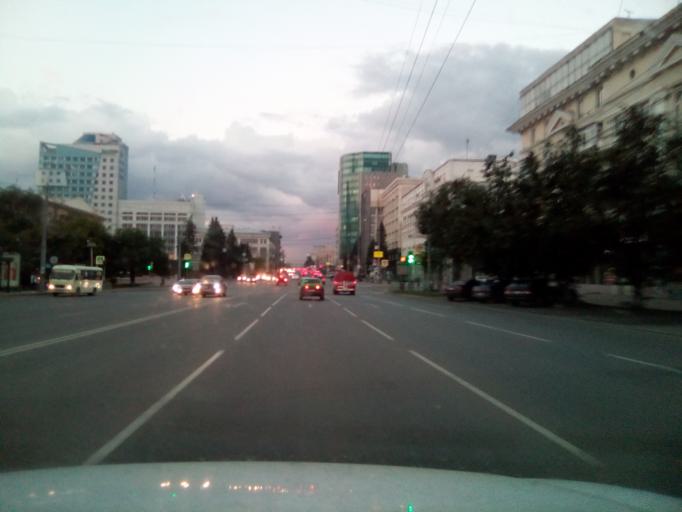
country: RU
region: Chelyabinsk
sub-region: Gorod Chelyabinsk
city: Chelyabinsk
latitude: 55.1600
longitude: 61.3949
